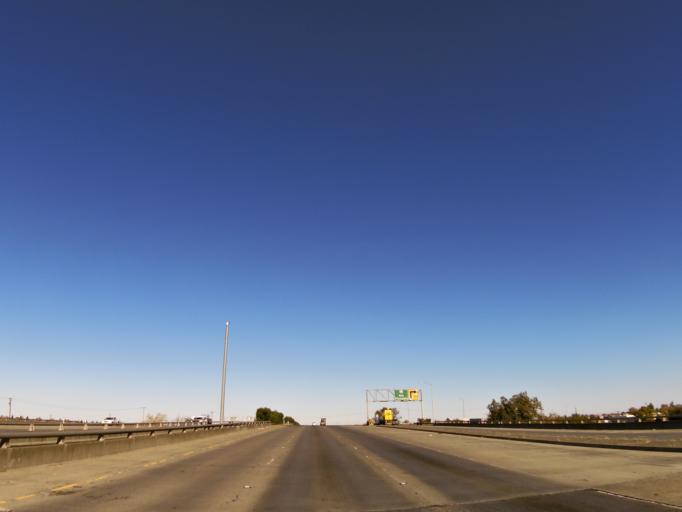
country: US
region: California
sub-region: Yolo County
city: West Sacramento
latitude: 38.6245
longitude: -121.5168
